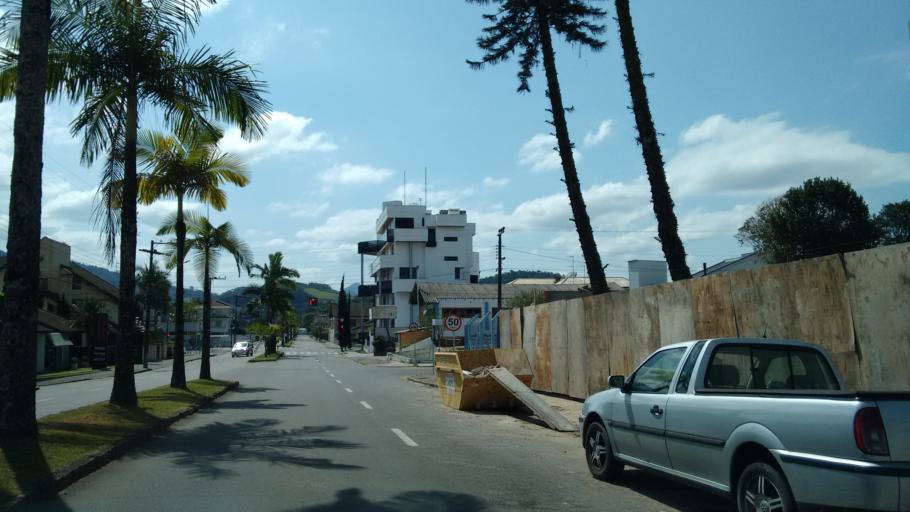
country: BR
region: Santa Catarina
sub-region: Pomerode
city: Pomerode
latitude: -26.7324
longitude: -49.1791
